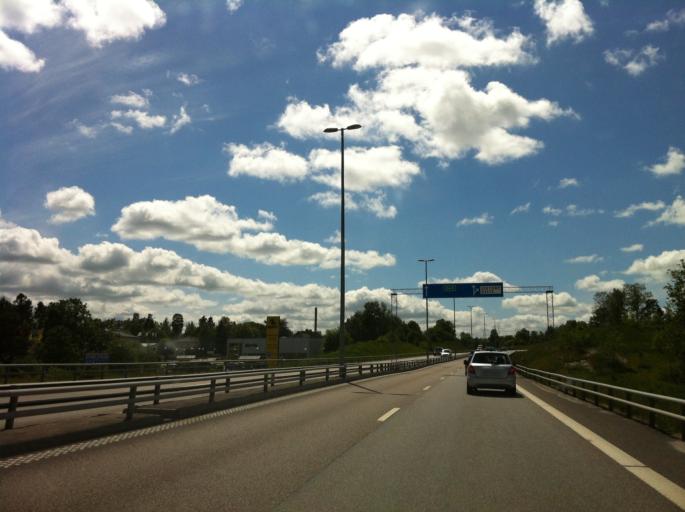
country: SE
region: Vaestra Goetaland
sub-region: Trollhattan
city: Trollhattan
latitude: 58.2616
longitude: 12.2890
